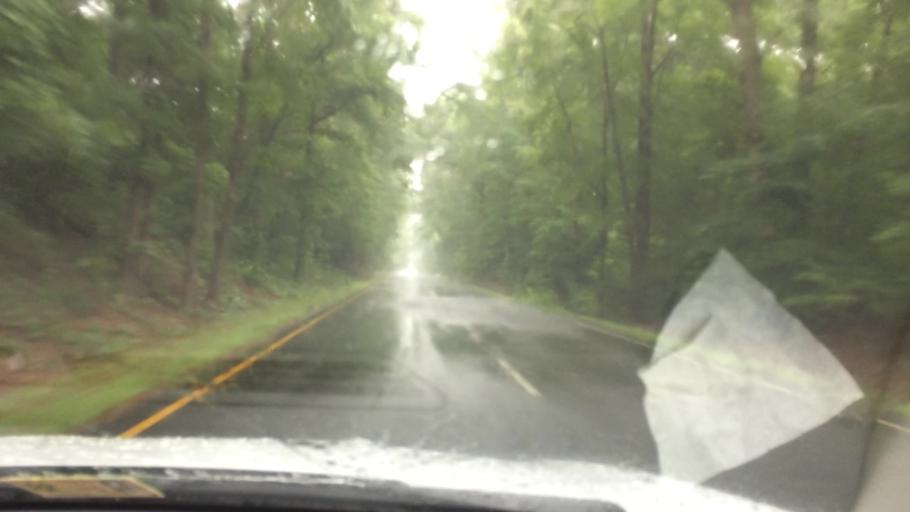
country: US
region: Virginia
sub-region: James City County
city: Williamsburg
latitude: 37.3945
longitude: -76.7799
